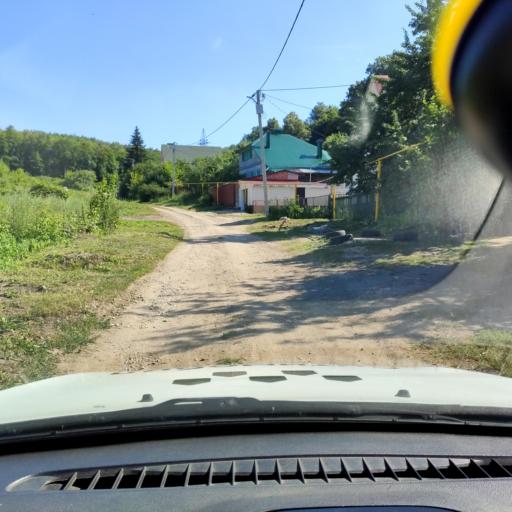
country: RU
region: Samara
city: Zhigulevsk
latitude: 53.3936
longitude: 49.5296
